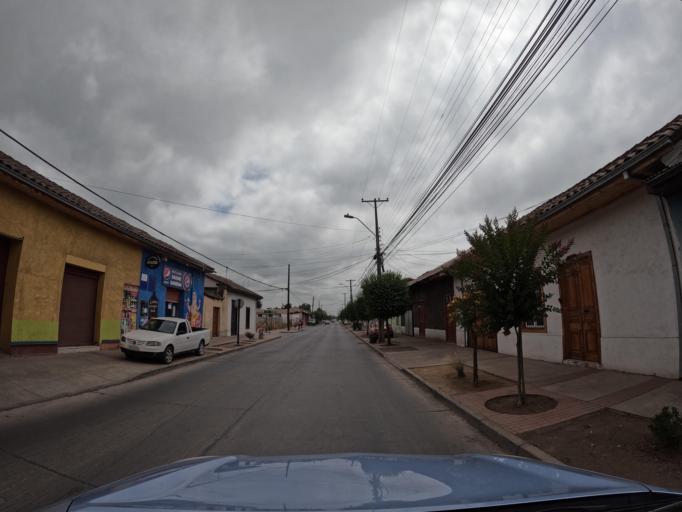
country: CL
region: O'Higgins
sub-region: Provincia de Colchagua
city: Chimbarongo
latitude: -34.7127
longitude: -71.0464
